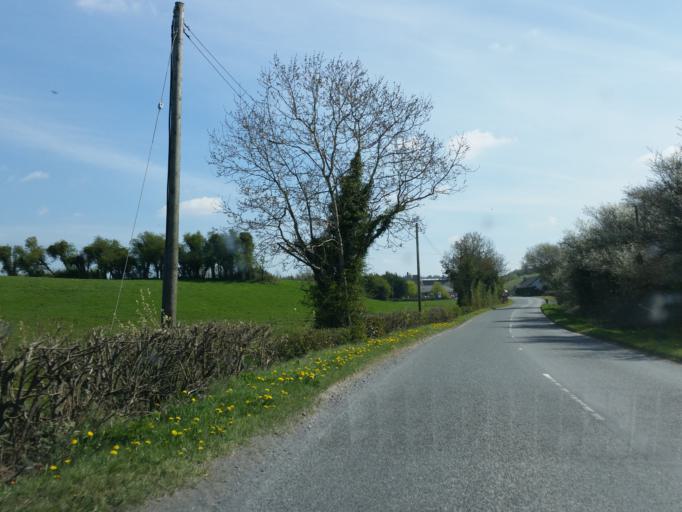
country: GB
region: Northern Ireland
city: Lisnaskea
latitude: 54.2703
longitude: -7.4346
